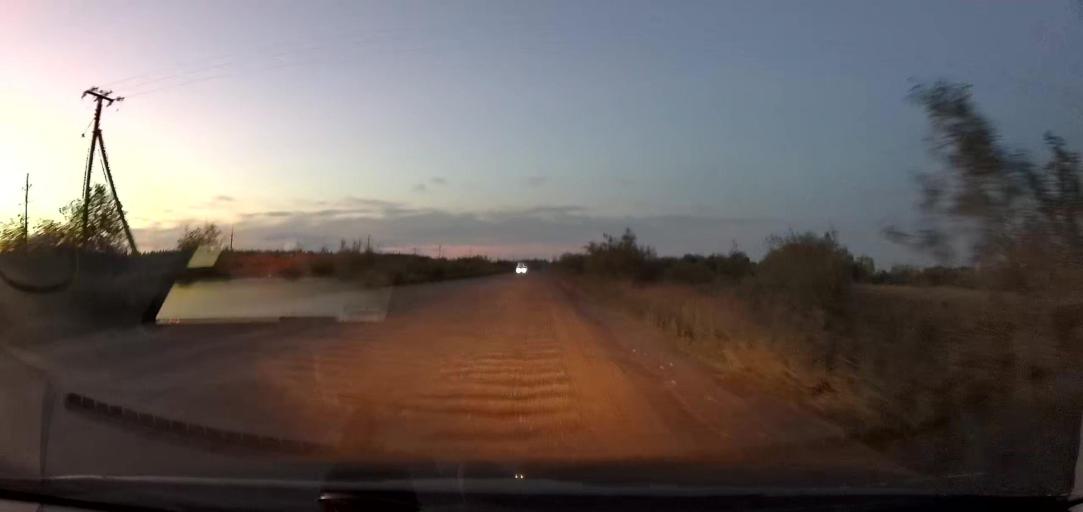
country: RU
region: Arkhangelskaya
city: Kholmogory
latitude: 64.3300
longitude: 41.4450
